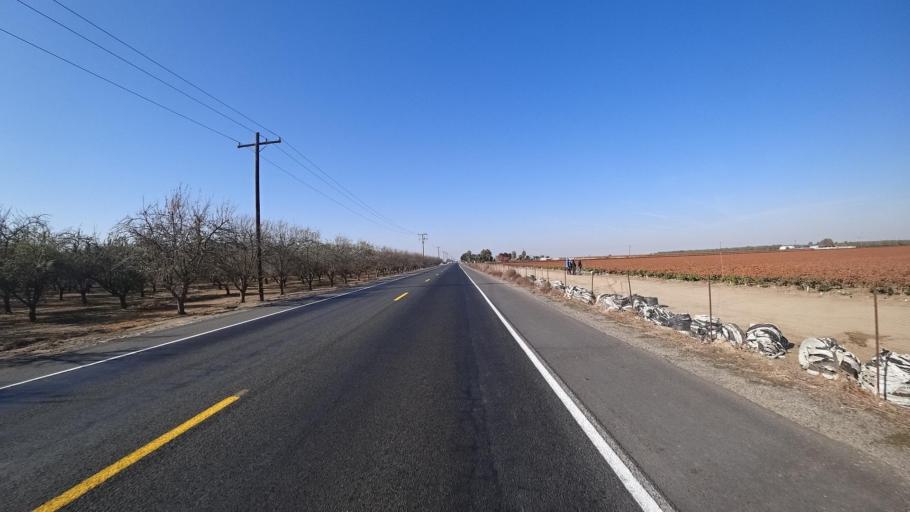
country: US
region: California
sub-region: Kern County
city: McFarland
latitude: 35.7179
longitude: -119.2550
